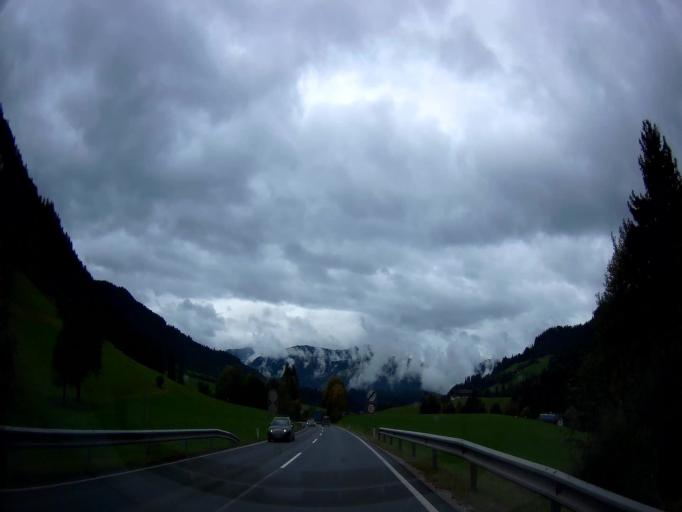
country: AT
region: Tyrol
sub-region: Politischer Bezirk Kufstein
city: Soll
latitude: 47.4928
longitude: 12.1688
